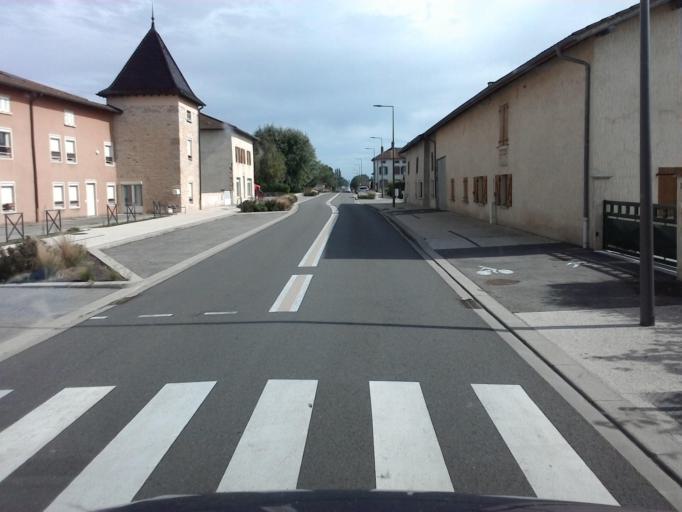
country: FR
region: Rhone-Alpes
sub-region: Departement de l'Ain
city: Mezeriat
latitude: 46.2561
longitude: 5.0562
